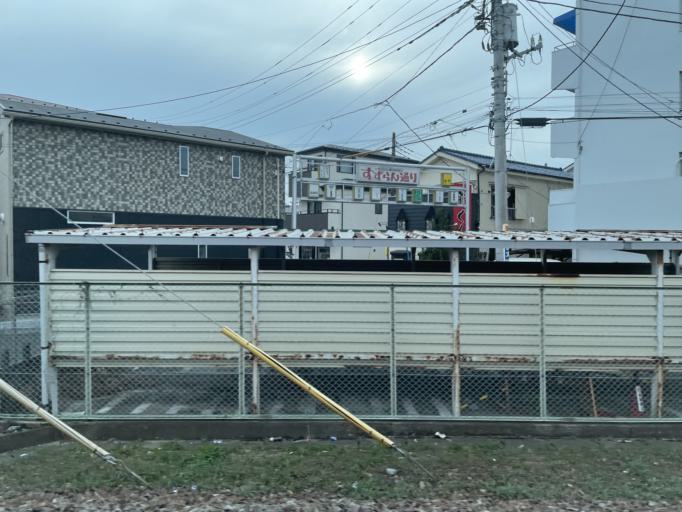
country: JP
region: Saitama
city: Kasukabe
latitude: 35.9630
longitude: 139.7664
